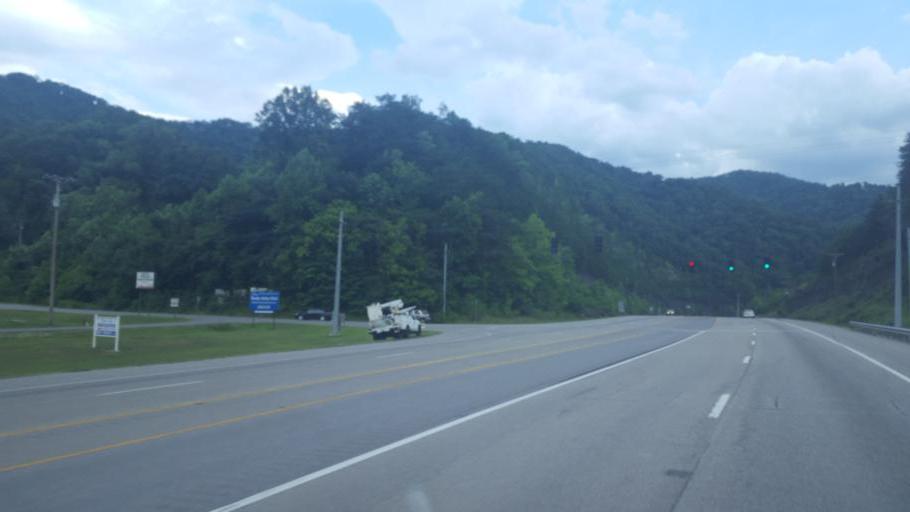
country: US
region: Kentucky
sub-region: Pike County
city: Pikeville
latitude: 37.3798
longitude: -82.5408
